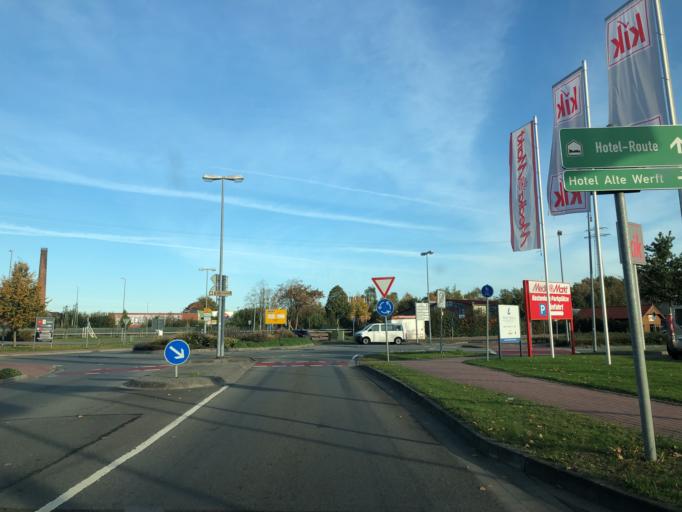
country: DE
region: Lower Saxony
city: Papenburg
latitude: 53.0854
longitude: 7.3839
